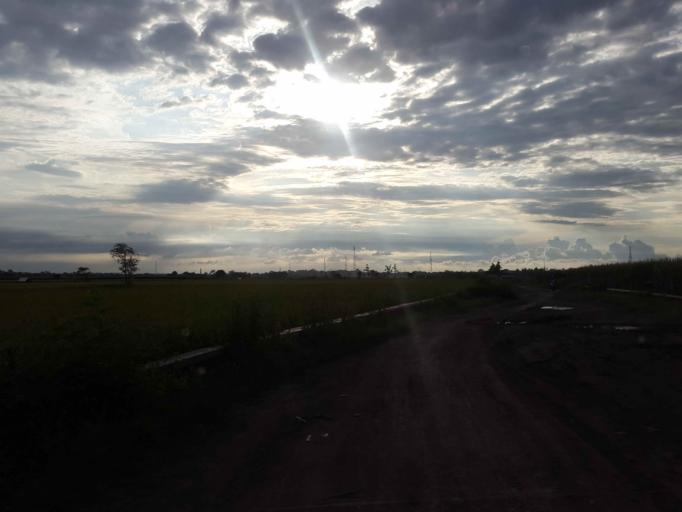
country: ID
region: Central Java
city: Ketanggungan
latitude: -6.9368
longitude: 108.9087
